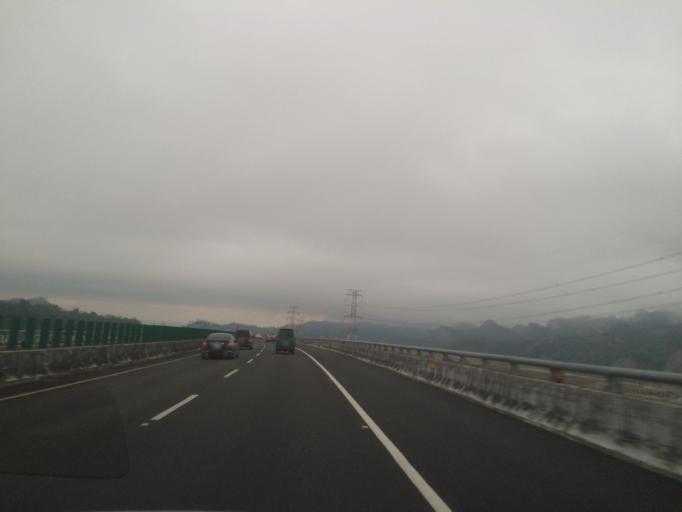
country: TW
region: Taiwan
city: Zhongxing New Village
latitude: 23.9945
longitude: 120.7500
